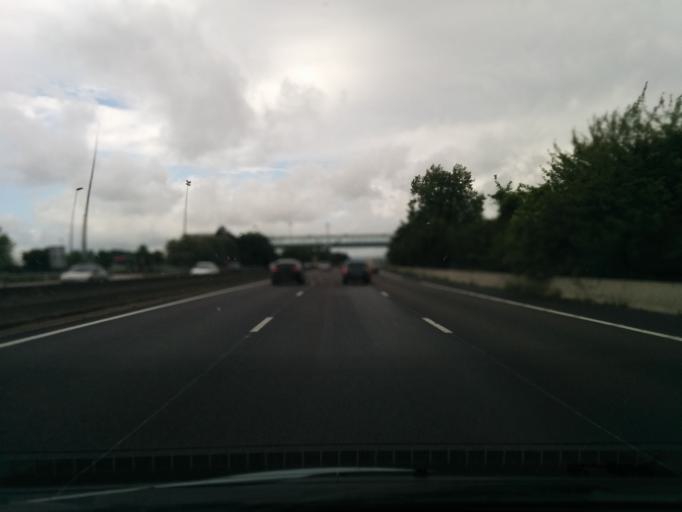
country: FR
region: Ile-de-France
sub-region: Departement des Yvelines
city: Morainvilliers
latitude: 48.9405
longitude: 1.9540
